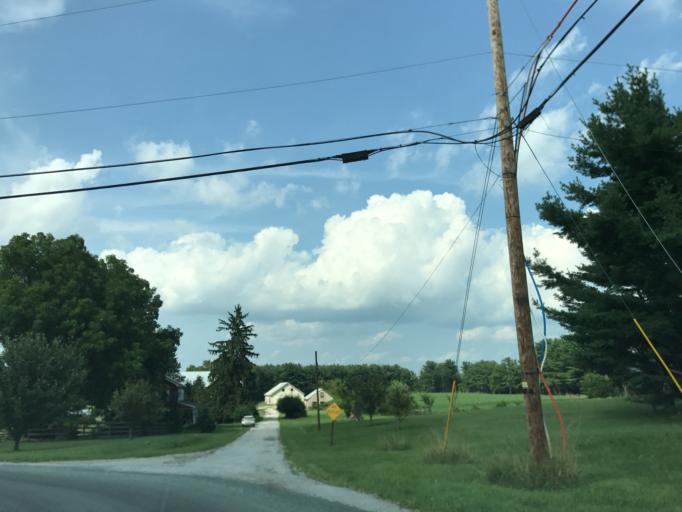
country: US
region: Pennsylvania
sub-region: York County
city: Pennville
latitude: 39.7488
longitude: -76.9987
